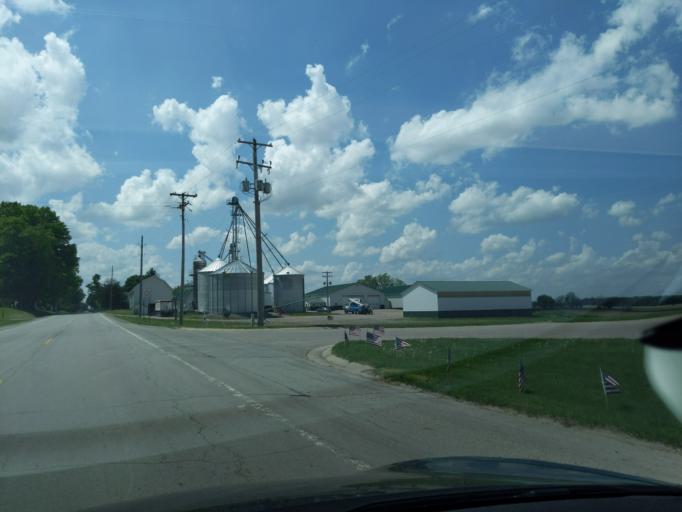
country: US
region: Michigan
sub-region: Ingham County
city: Williamston
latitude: 42.5559
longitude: -84.2936
